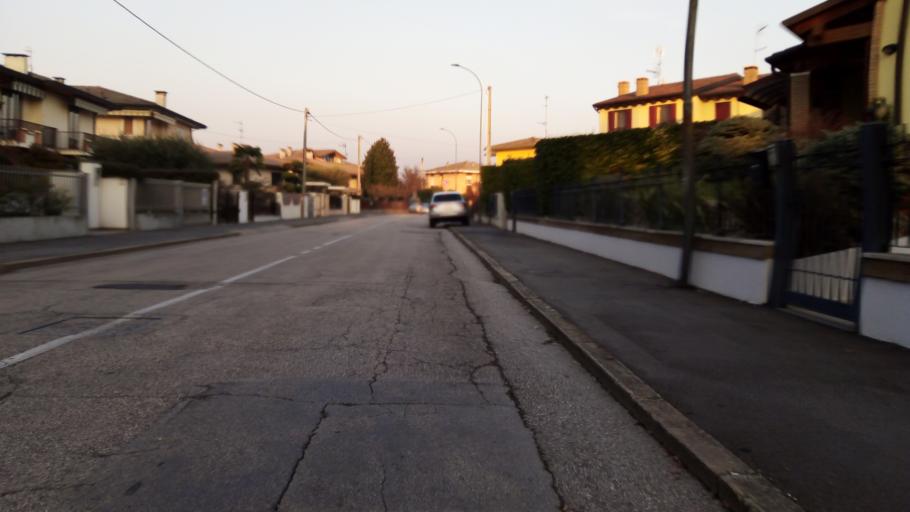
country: IT
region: Veneto
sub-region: Provincia di Padova
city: Abano Terme
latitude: 45.3547
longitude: 11.7612
